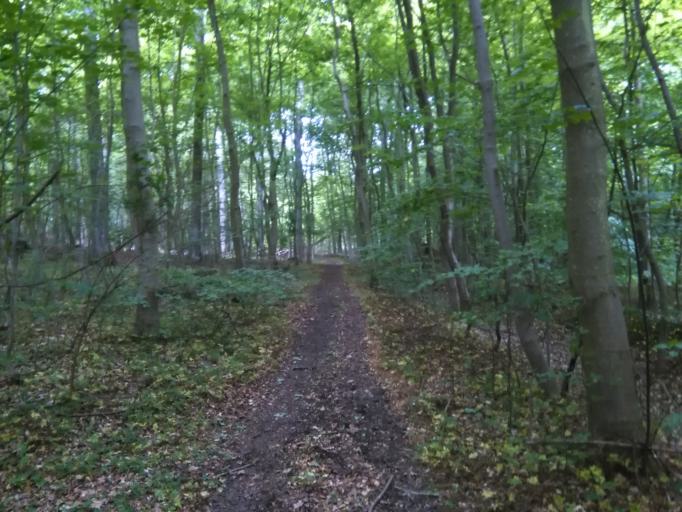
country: DK
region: Central Jutland
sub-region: Arhus Kommune
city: Beder
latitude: 56.0587
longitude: 10.2527
